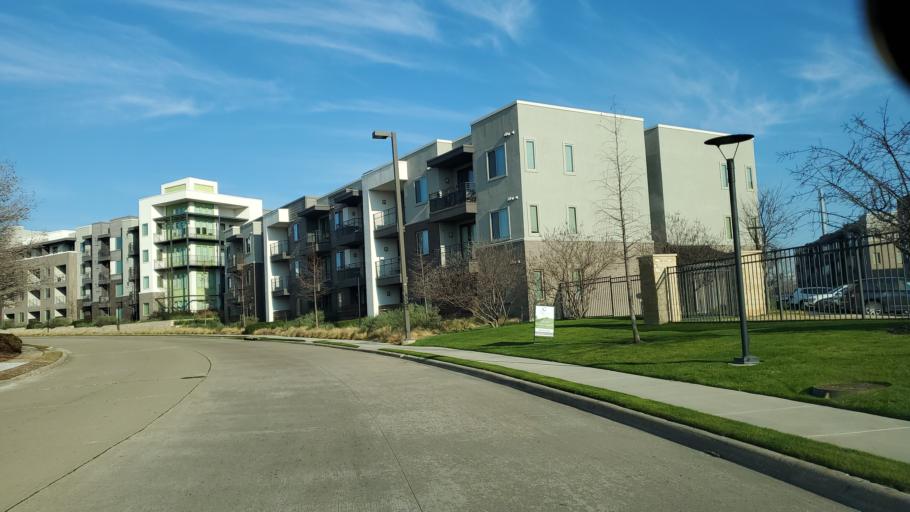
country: US
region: Texas
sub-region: Collin County
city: Plano
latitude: 33.0051
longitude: -96.7042
